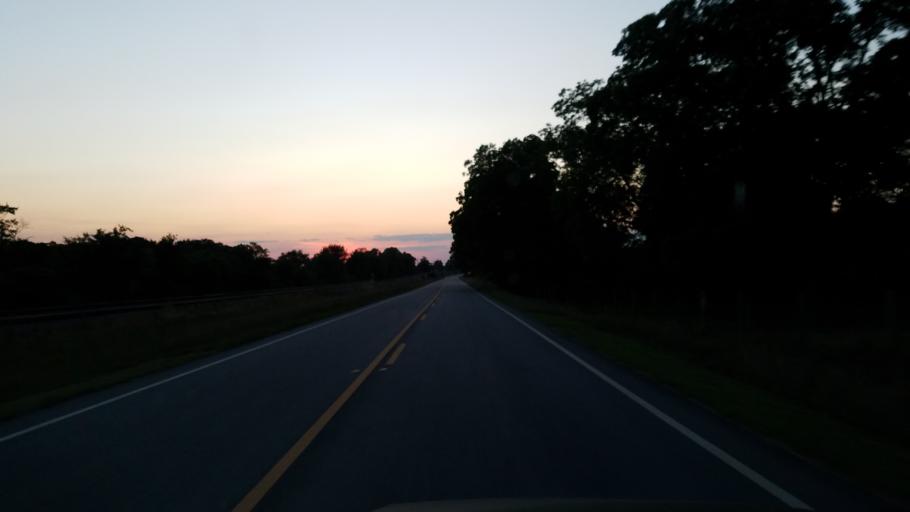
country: US
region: Georgia
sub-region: Turner County
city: Ashburn
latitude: 31.6484
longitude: -83.6232
